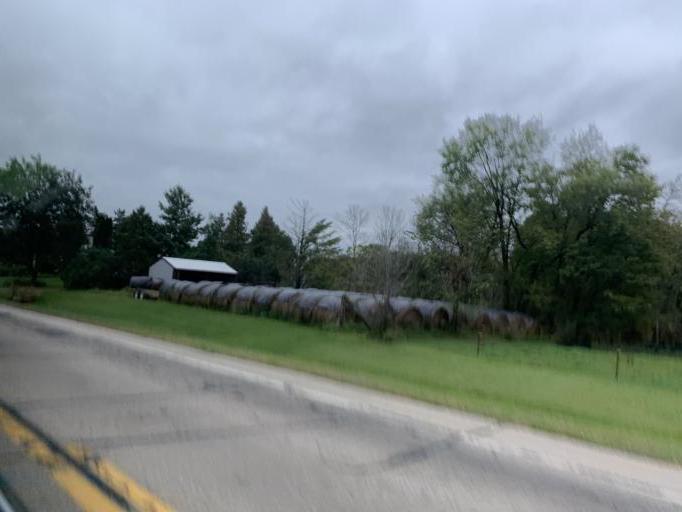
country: US
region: Wisconsin
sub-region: Grant County
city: Muscoda
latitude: 43.2198
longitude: -90.5527
